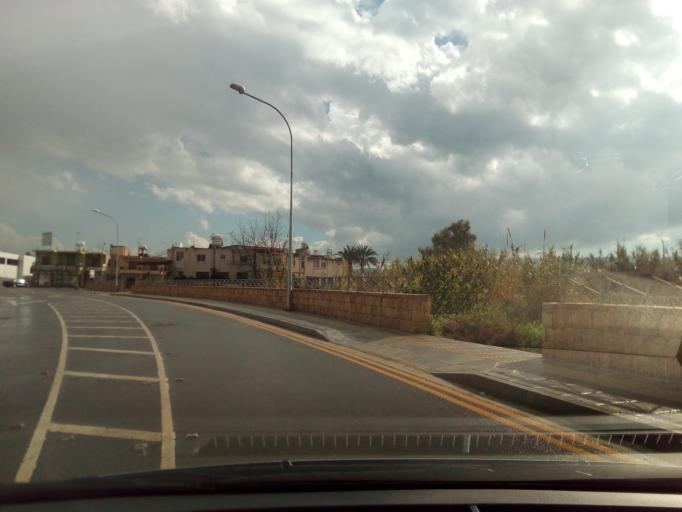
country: CY
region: Pafos
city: Polis
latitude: 35.0325
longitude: 32.4229
